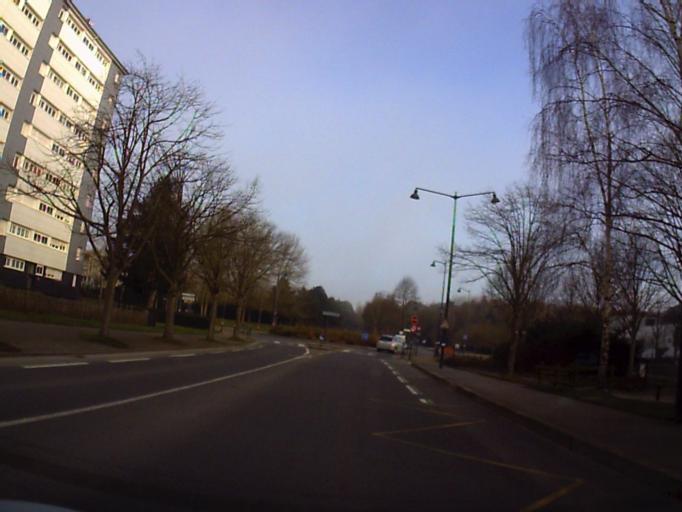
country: FR
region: Brittany
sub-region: Departement d'Ille-et-Vilaine
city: Rennes
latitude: 48.1316
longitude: -1.6520
